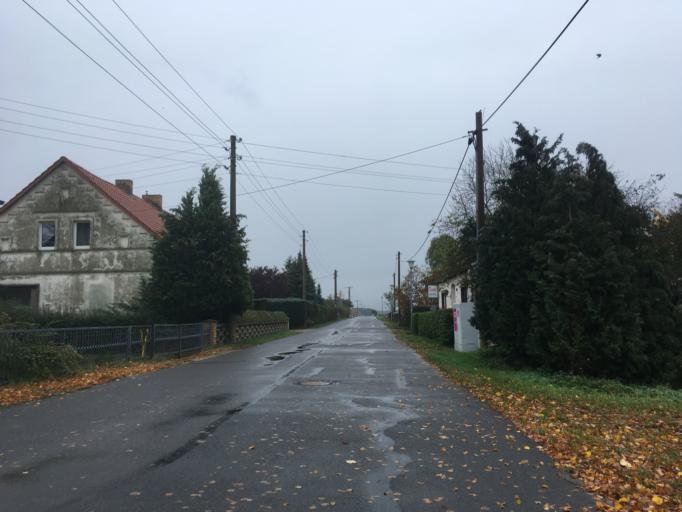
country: DE
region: Brandenburg
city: Neu Zauche
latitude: 52.0170
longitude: 14.1451
